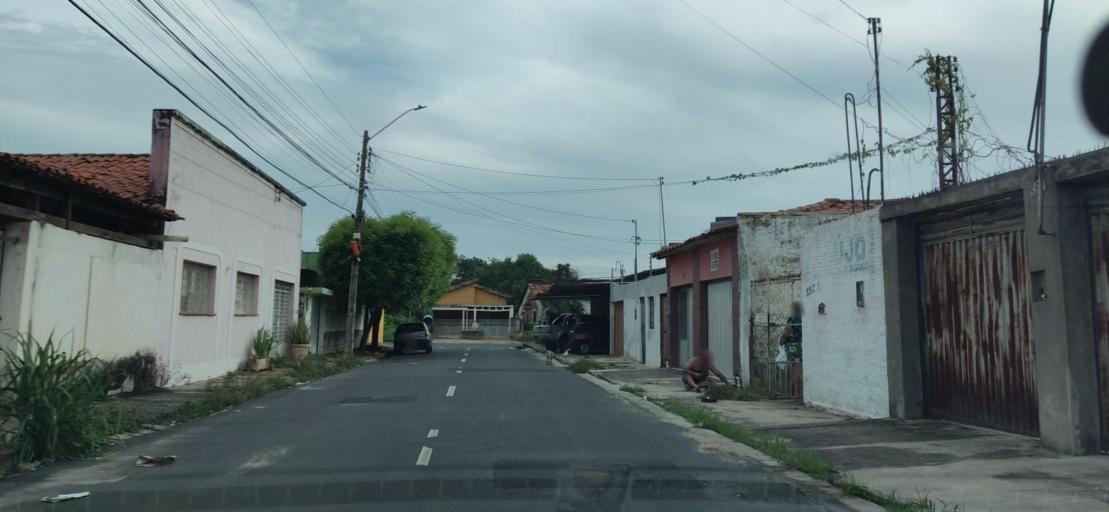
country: BR
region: Piaui
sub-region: Teresina
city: Teresina
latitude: -5.0972
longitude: -42.7987
